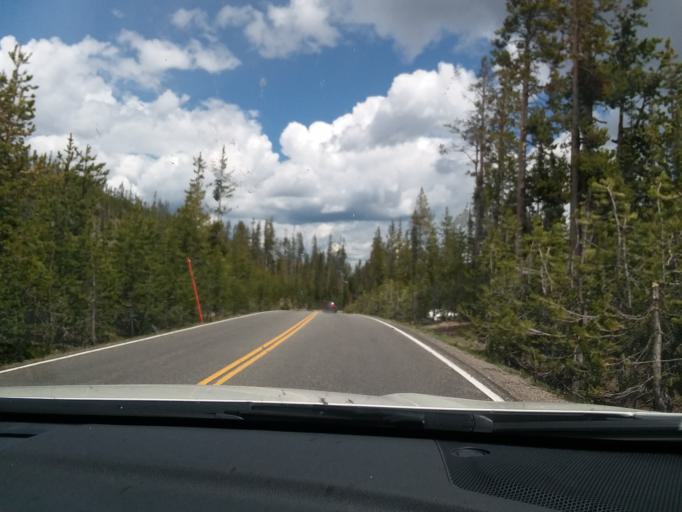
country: US
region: Montana
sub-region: Gallatin County
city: West Yellowstone
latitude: 44.2386
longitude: -110.6496
